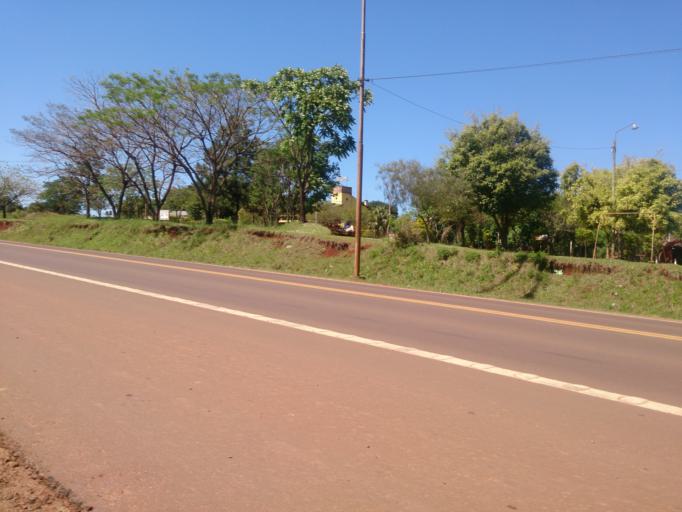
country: AR
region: Misiones
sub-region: Departamento de Obera
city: Obera
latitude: -27.4970
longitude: -55.1064
